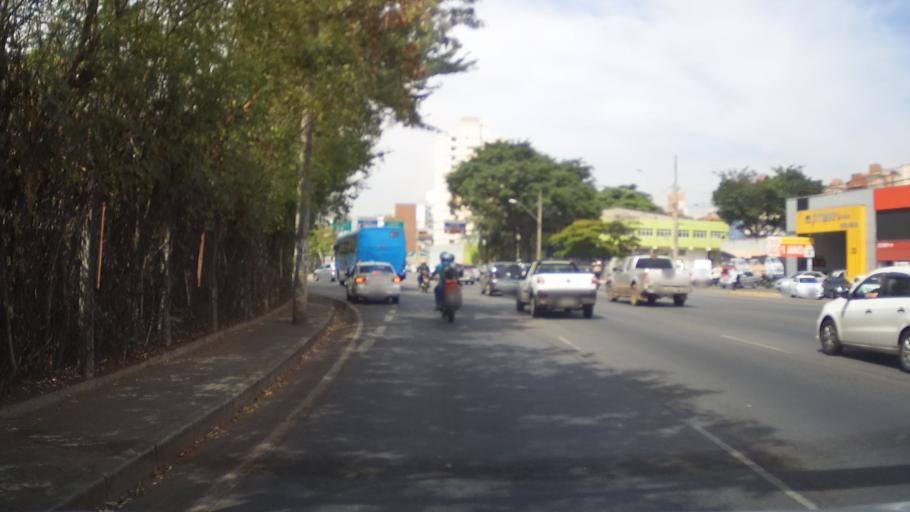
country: BR
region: Minas Gerais
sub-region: Belo Horizonte
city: Belo Horizonte
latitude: -19.9231
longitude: -43.9851
